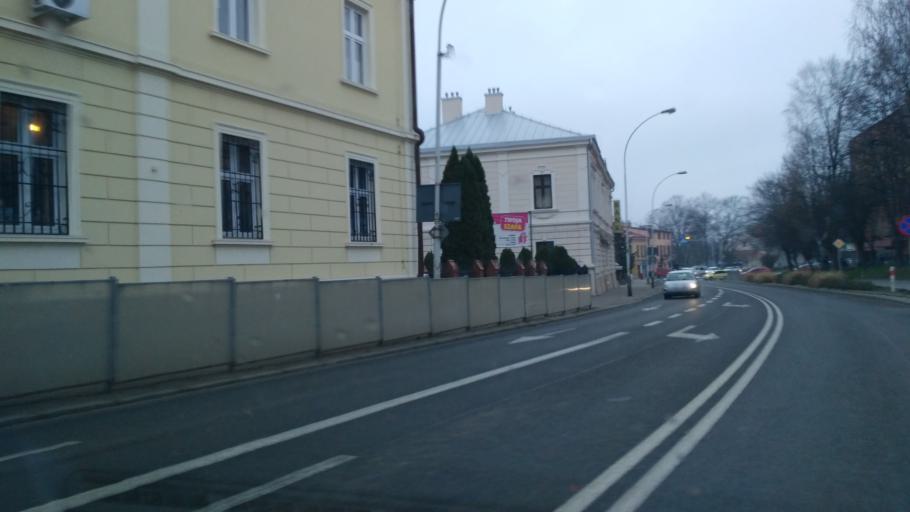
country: PL
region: Subcarpathian Voivodeship
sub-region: Powiat przeworski
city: Przeworsk
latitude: 50.0588
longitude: 22.4899
